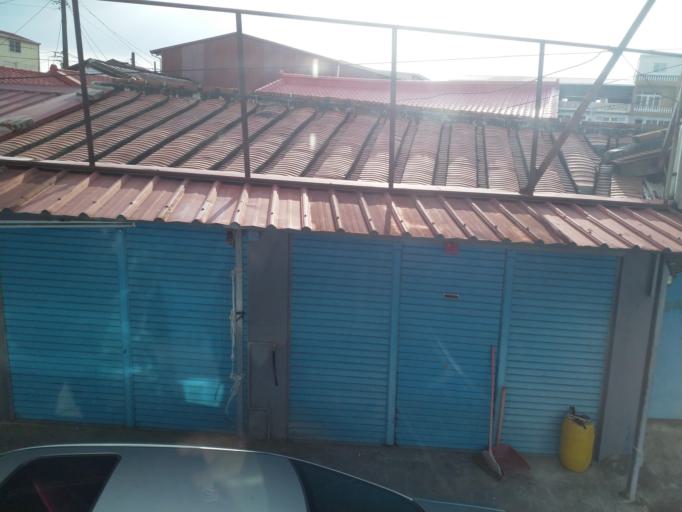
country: TW
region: Taiwan
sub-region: Pingtung
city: Pingtung
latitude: 22.8978
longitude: 120.5428
